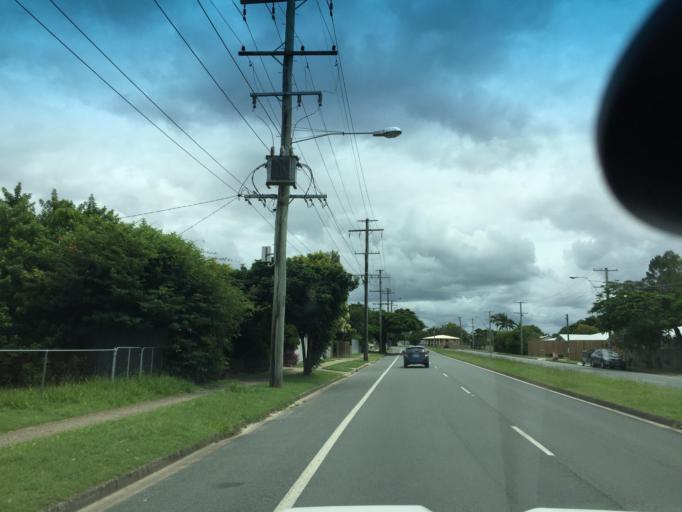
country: AU
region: Queensland
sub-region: Moreton Bay
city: Caboolture
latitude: -27.0832
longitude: 152.9374
